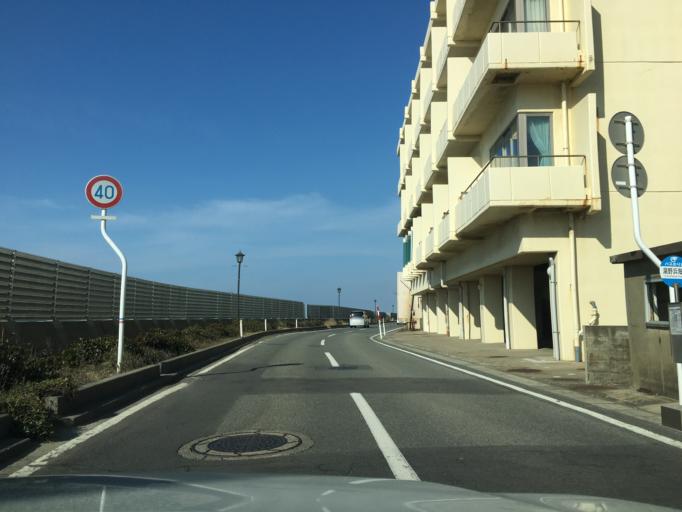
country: JP
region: Yamagata
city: Tsuruoka
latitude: 38.7801
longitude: 139.7511
